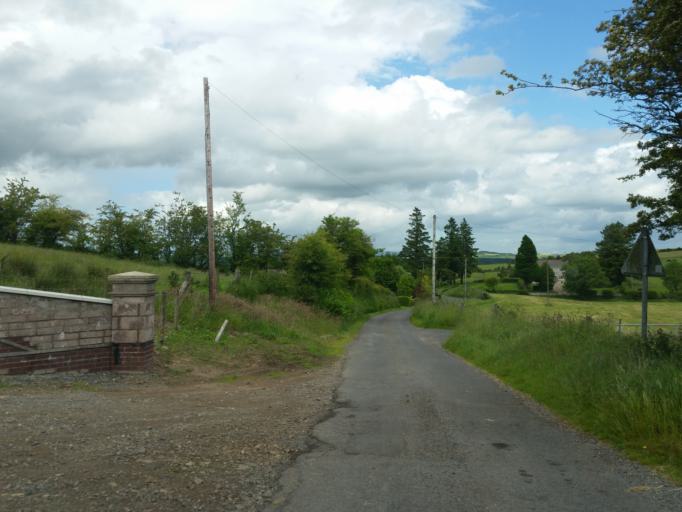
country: GB
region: Northern Ireland
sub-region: Omagh District
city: Omagh
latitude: 54.5597
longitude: -7.0571
